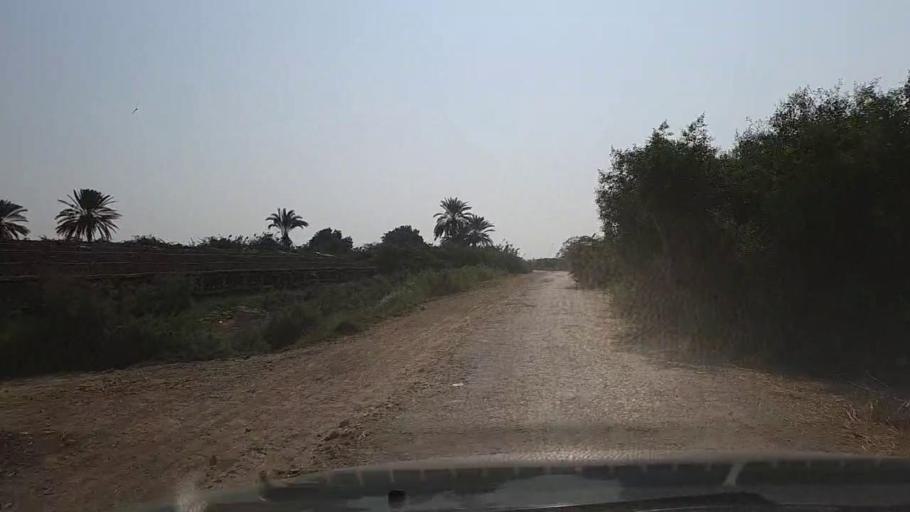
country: PK
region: Sindh
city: Mirpur Sakro
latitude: 24.3924
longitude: 67.6650
